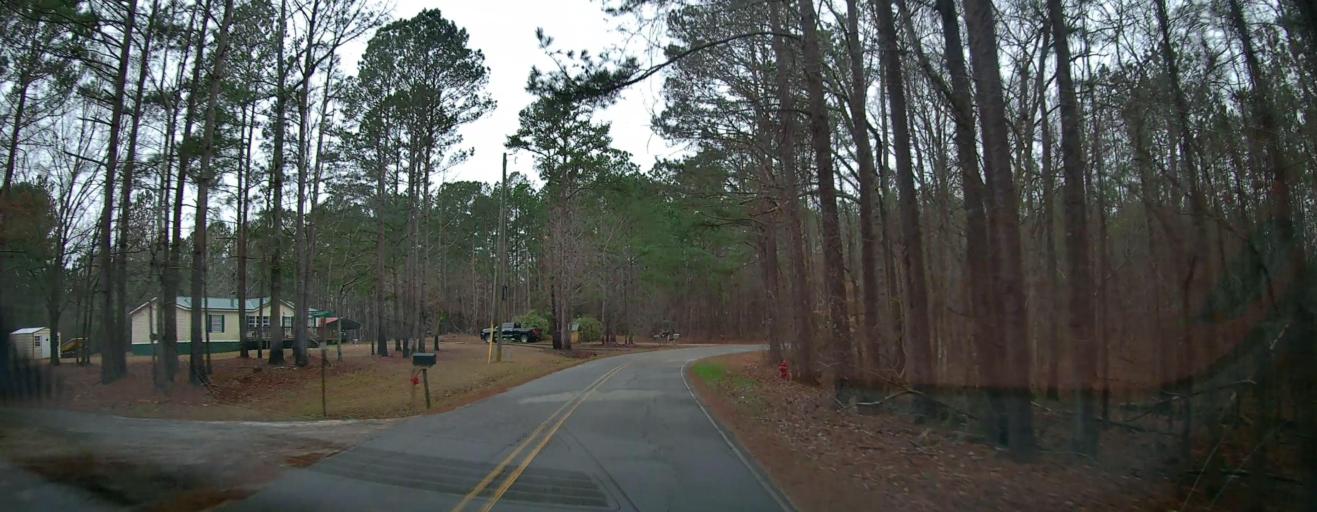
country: US
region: Georgia
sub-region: Monroe County
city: Forsyth
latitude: 33.0170
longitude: -83.8465
